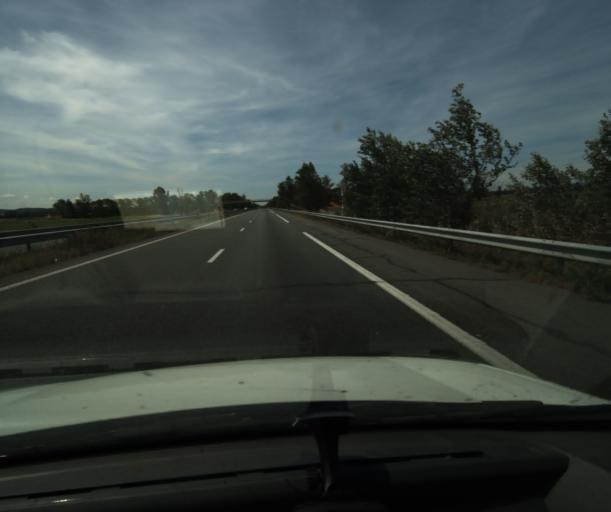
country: FR
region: Languedoc-Roussillon
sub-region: Departement de l'Aude
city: Saint-Martin-Lalande
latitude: 43.2654
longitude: 2.0147
